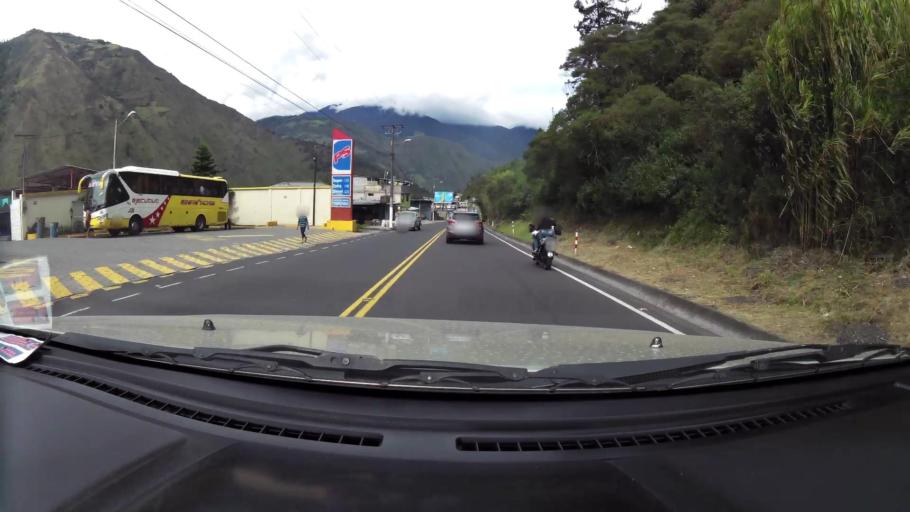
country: EC
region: Tungurahua
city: Banos
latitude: -1.4000
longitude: -78.4391
